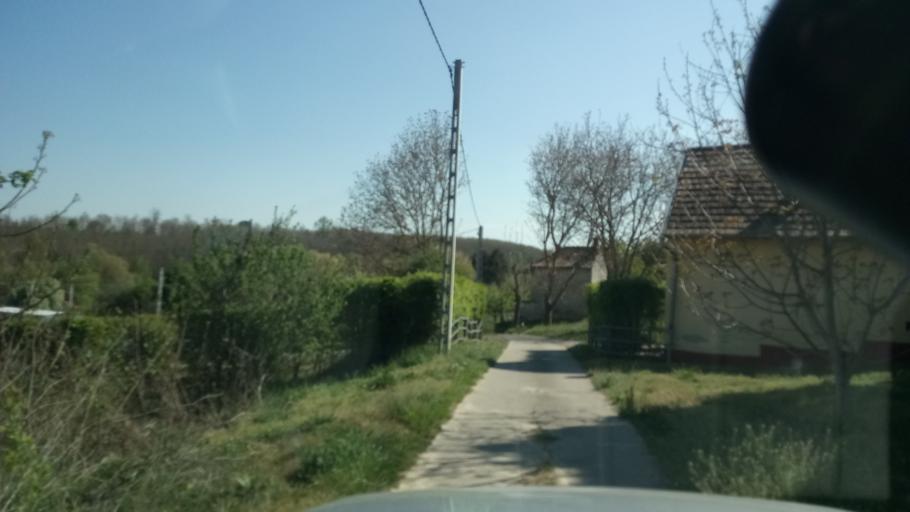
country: HU
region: Zala
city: Sarmellek
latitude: 46.6974
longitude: 17.1005
